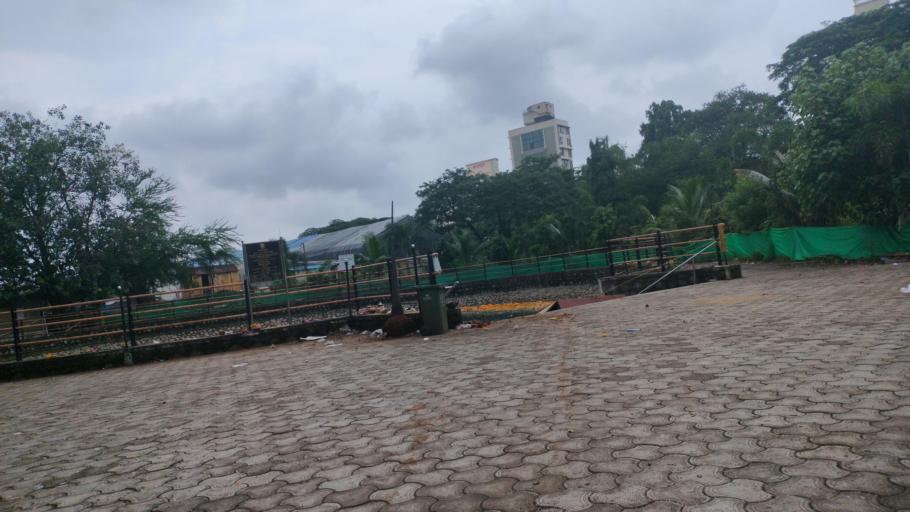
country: IN
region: Maharashtra
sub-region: Mumbai Suburban
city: Borivli
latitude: 19.2214
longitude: 72.8457
